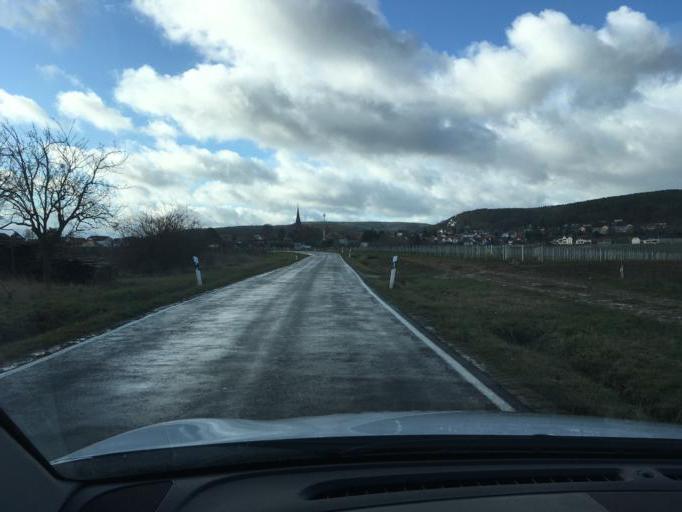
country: DE
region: Rheinland-Pfalz
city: Weisenheim am Berg
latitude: 49.5187
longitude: 8.1593
